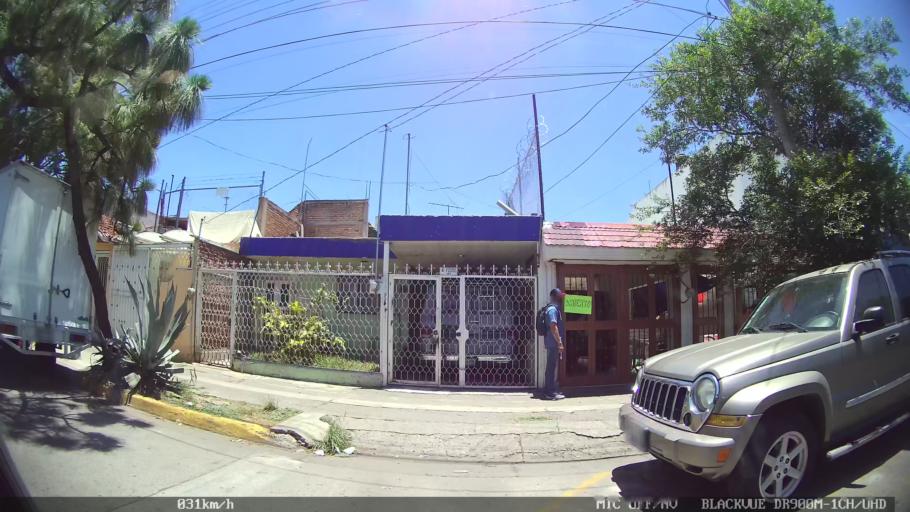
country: MX
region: Jalisco
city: Tlaquepaque
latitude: 20.6741
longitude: -103.2795
